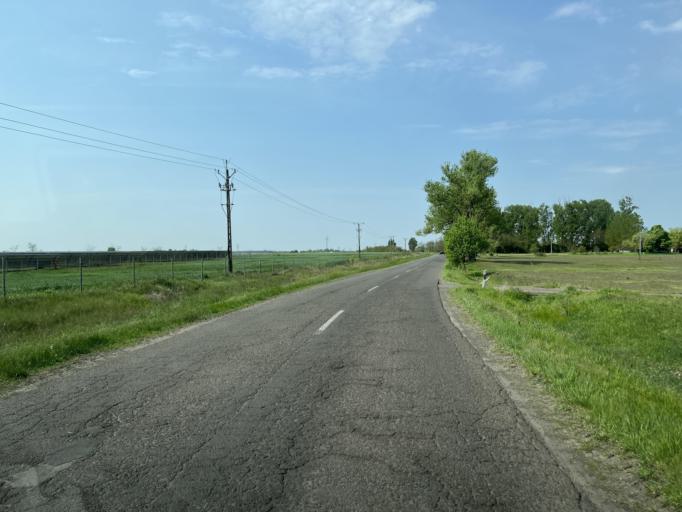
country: HU
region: Pest
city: Nagykoros
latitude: 47.0532
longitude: 19.8461
